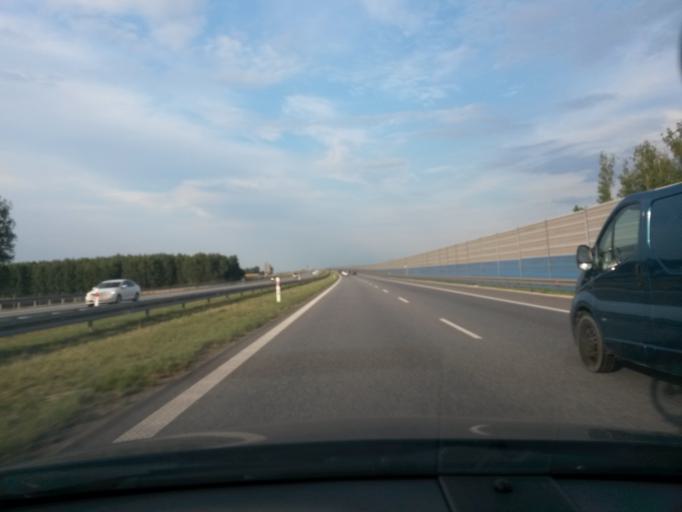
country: PL
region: Lodz Voivodeship
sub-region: Powiat brzezinski
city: Dmosin
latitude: 51.9012
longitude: 19.7188
